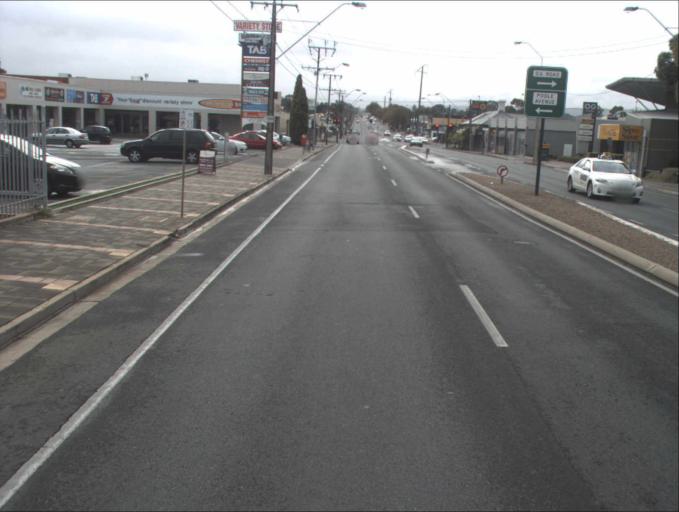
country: AU
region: South Australia
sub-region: Port Adelaide Enfield
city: Klemzig
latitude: -34.8754
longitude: 138.6315
